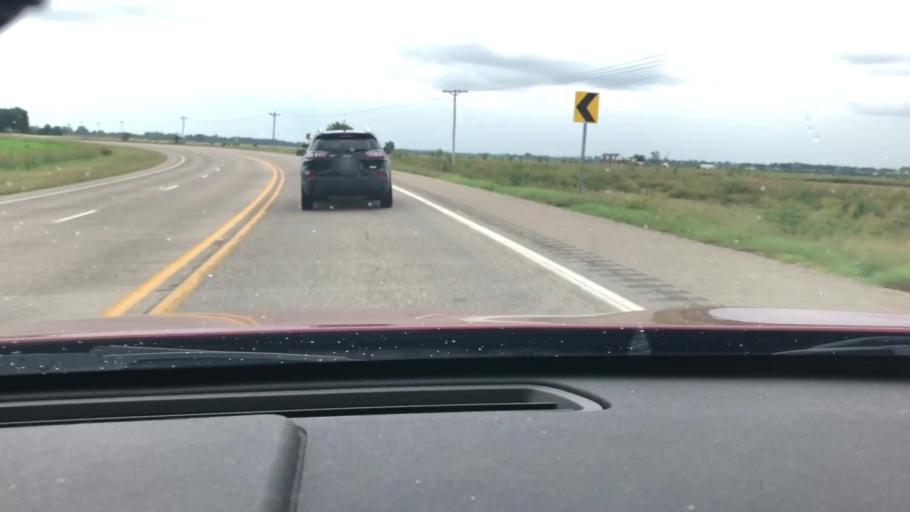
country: US
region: Arkansas
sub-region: Lafayette County
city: Lewisville
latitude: 33.3928
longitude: -93.7394
